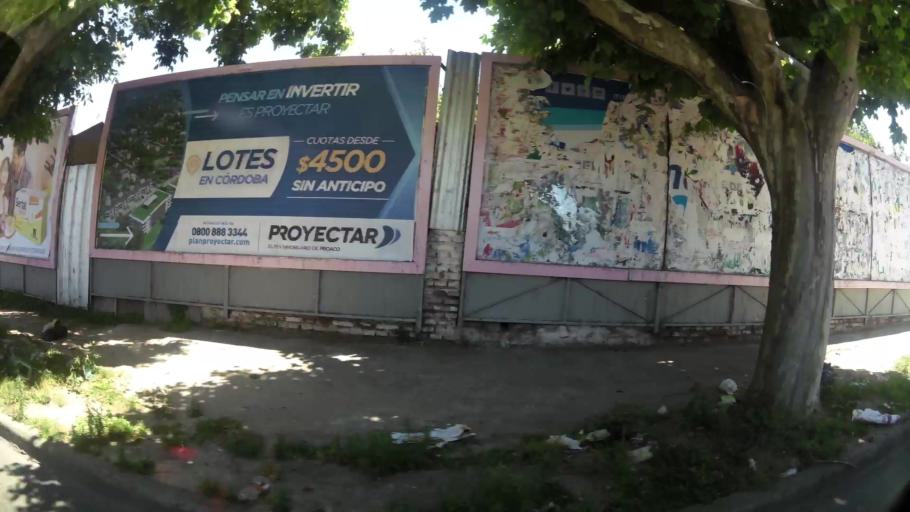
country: AR
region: Cordoba
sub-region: Departamento de Capital
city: Cordoba
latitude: -31.3996
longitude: -64.2047
